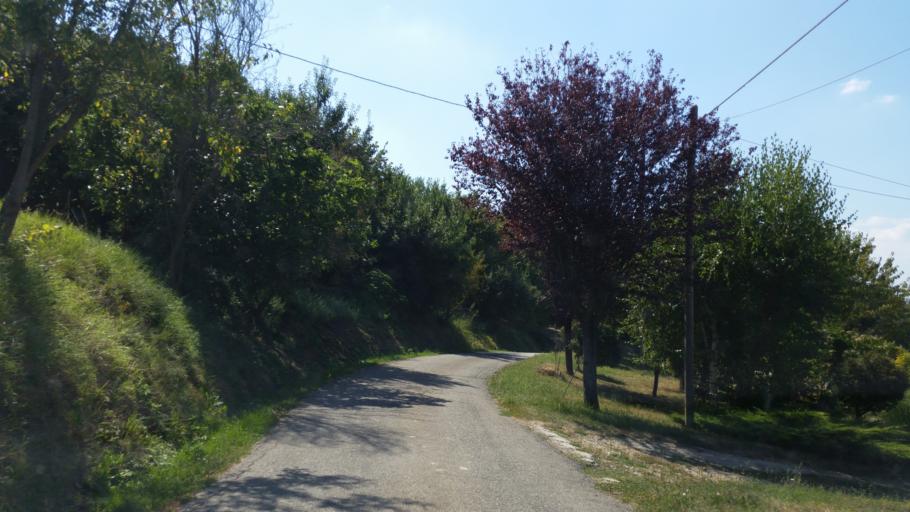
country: IT
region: Piedmont
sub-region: Provincia di Cuneo
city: Mango
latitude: 44.6673
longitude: 8.1368
